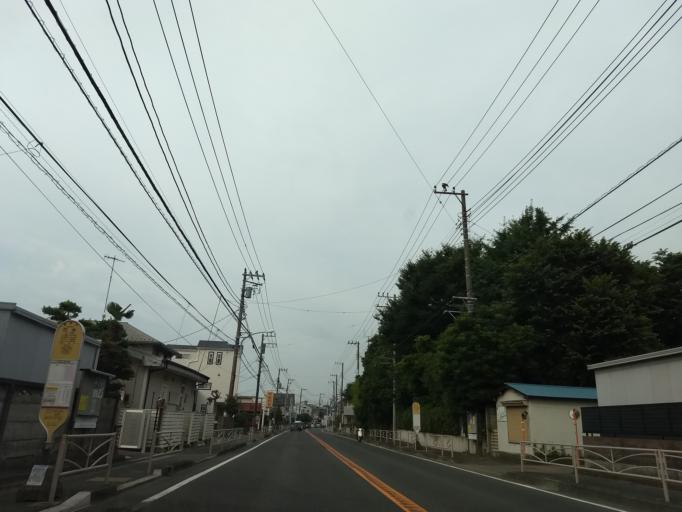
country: JP
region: Kanagawa
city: Hiratsuka
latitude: 35.3217
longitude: 139.3270
